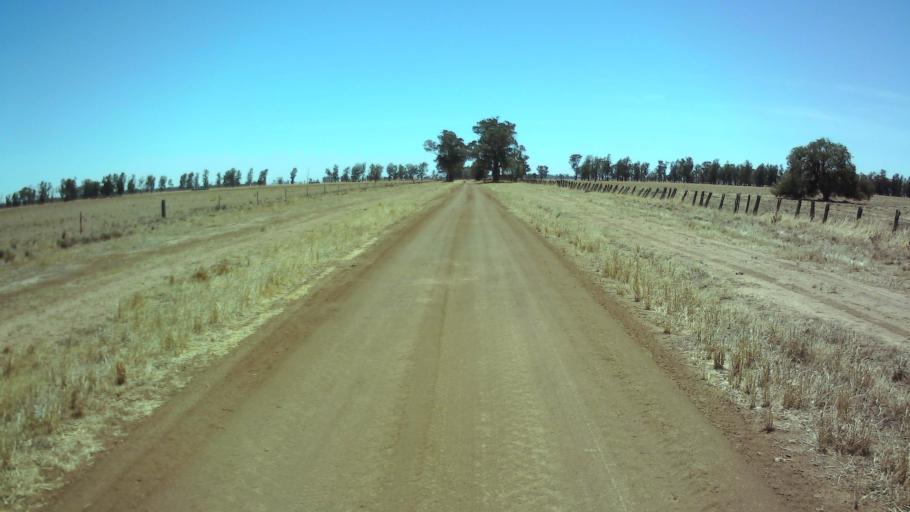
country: AU
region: New South Wales
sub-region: Weddin
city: Grenfell
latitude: -33.9735
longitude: 147.7376
